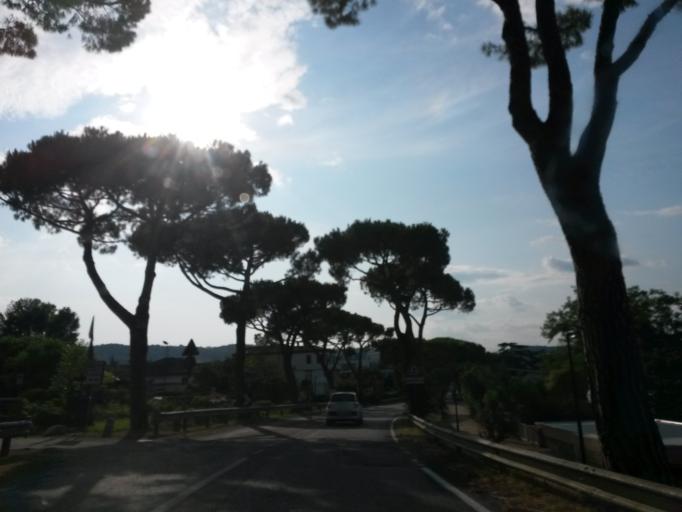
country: IT
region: Lombardy
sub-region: Provincia di Brescia
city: Padenghe sul Garda
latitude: 45.4898
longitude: 10.5247
